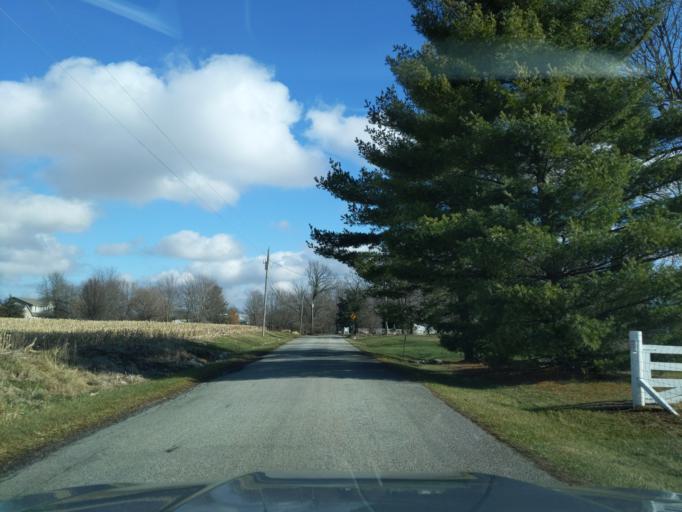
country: US
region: Indiana
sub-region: Decatur County
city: Greensburg
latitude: 39.2787
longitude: -85.4443
